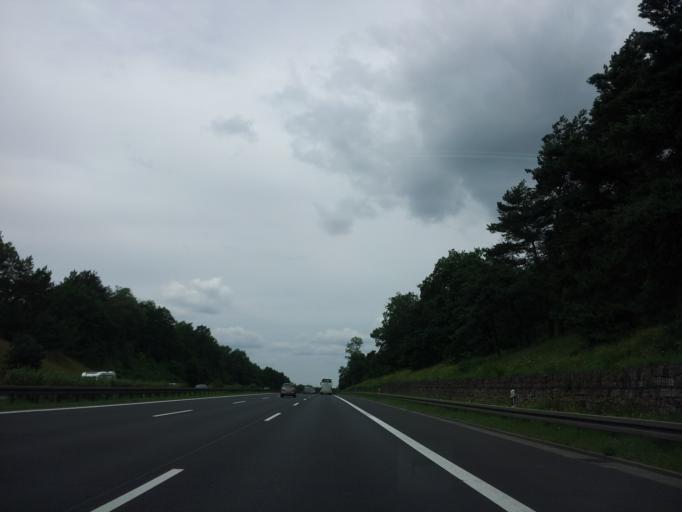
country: DE
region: Brandenburg
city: Rangsdorf
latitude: 52.3063
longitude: 13.4095
